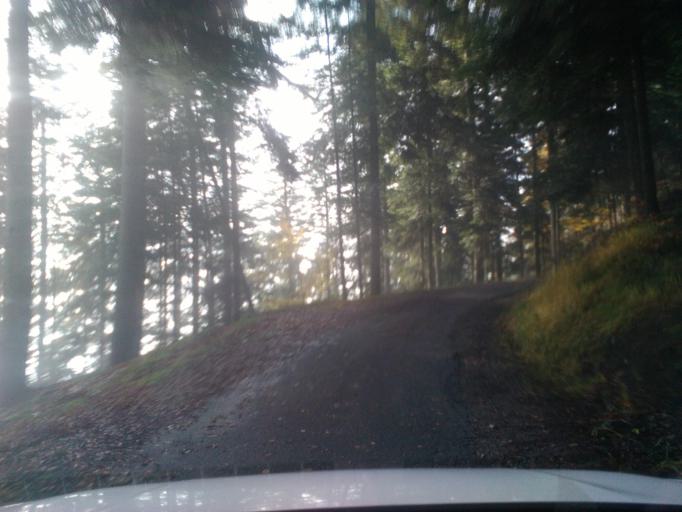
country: FR
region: Lorraine
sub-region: Departement des Vosges
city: Senones
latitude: 48.4114
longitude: 6.9747
